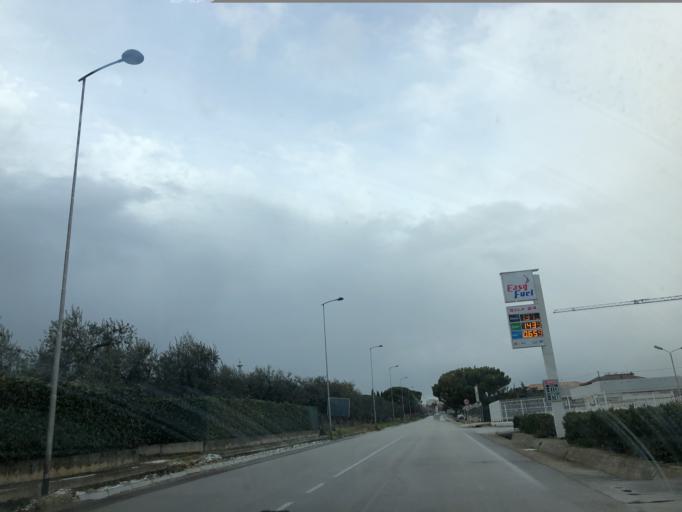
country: IT
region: Apulia
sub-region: Provincia di Foggia
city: Lucera
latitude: 41.5021
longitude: 15.3531
